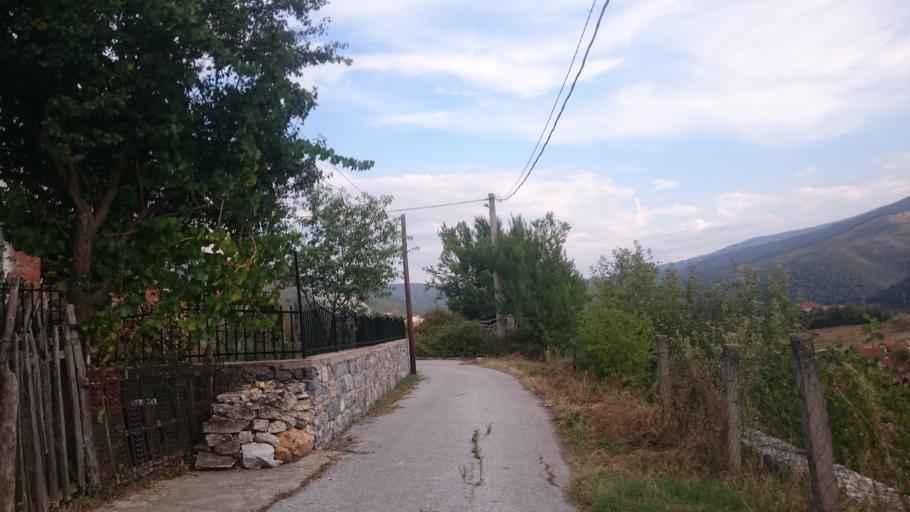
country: MK
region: Makedonski Brod
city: Makedonski Brod
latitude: 41.5200
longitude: 21.2147
